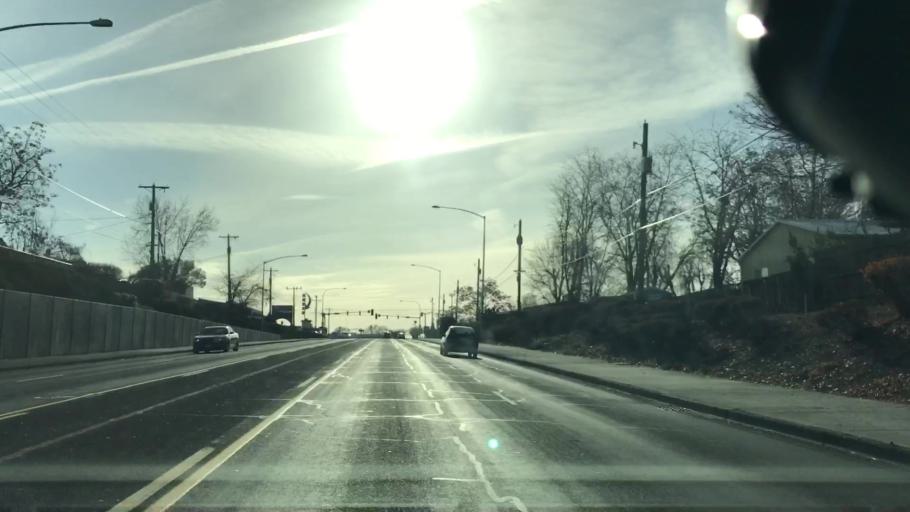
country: US
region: Washington
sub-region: Grant County
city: Moses Lake
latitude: 47.1231
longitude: -119.2682
